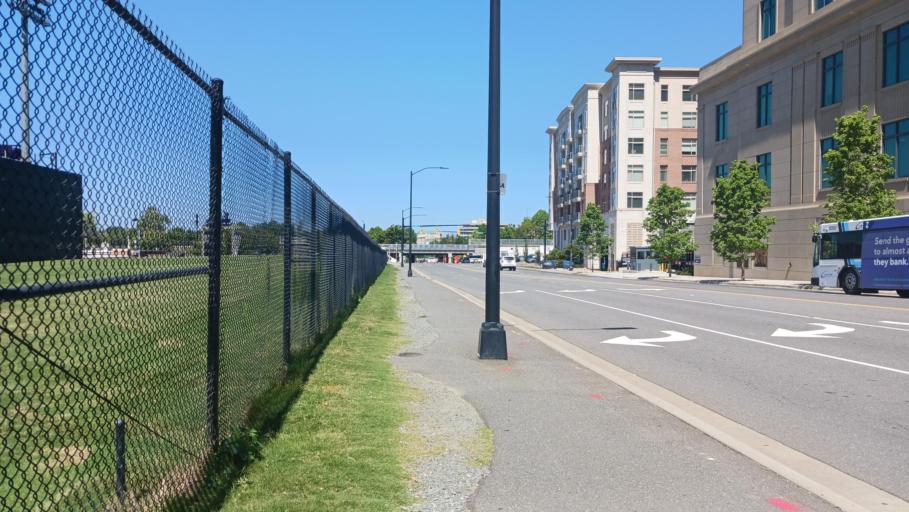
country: US
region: North Carolina
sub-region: Mecklenburg County
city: Charlotte
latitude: 35.2287
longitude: -80.8471
